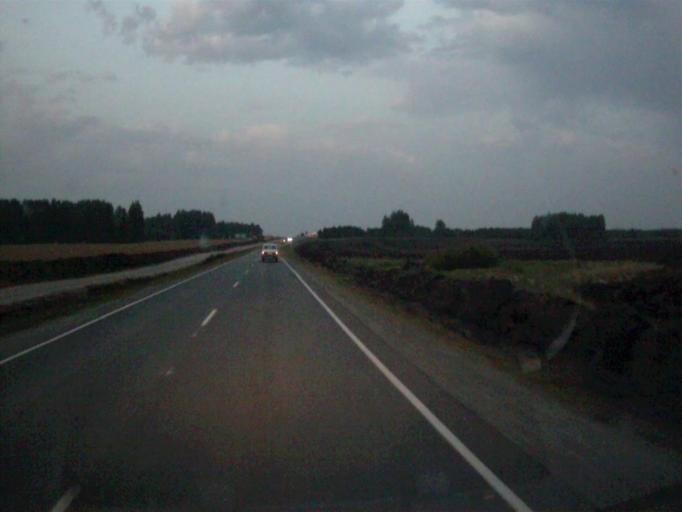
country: RU
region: Chelyabinsk
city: Argayash
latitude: 55.2085
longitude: 60.8226
